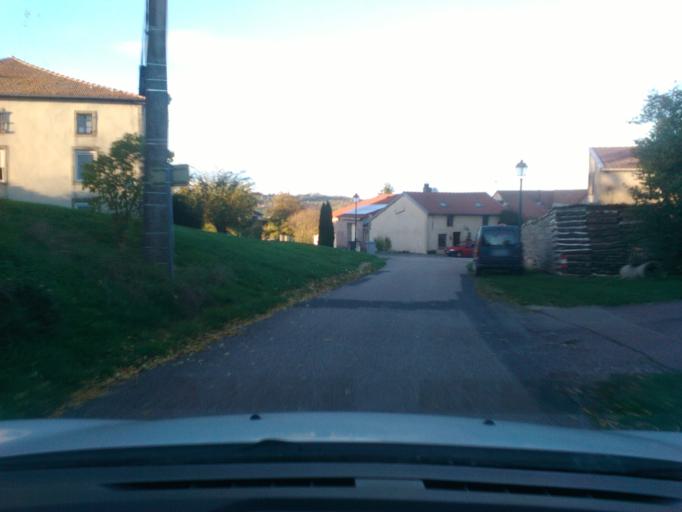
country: FR
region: Lorraine
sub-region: Departement des Vosges
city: Charmes
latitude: 48.3468
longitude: 6.2530
